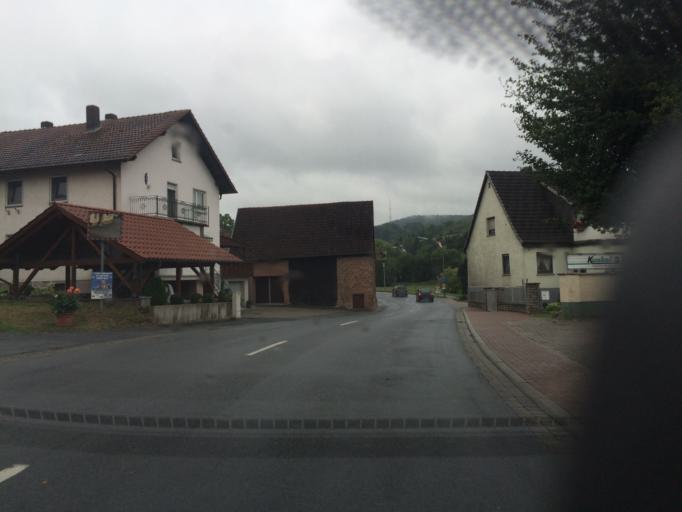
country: DE
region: Bavaria
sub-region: Regierungsbezirk Unterfranken
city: Haibach
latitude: 49.9588
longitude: 9.2486
